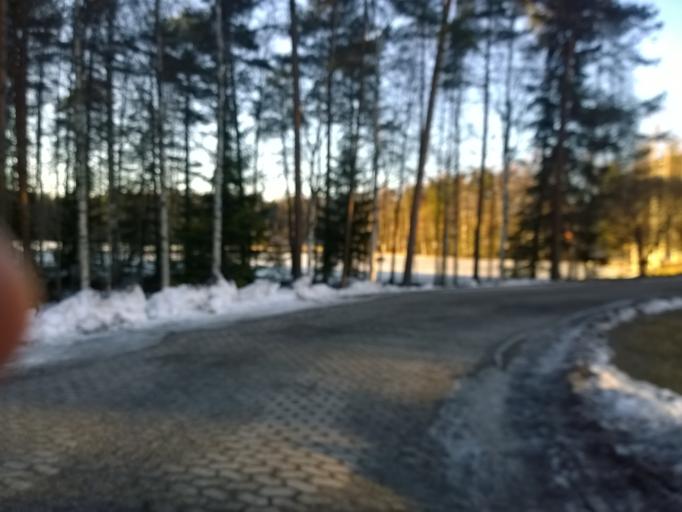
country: FI
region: Pirkanmaa
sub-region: Tampere
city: Tampere
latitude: 61.4477
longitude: 23.8490
